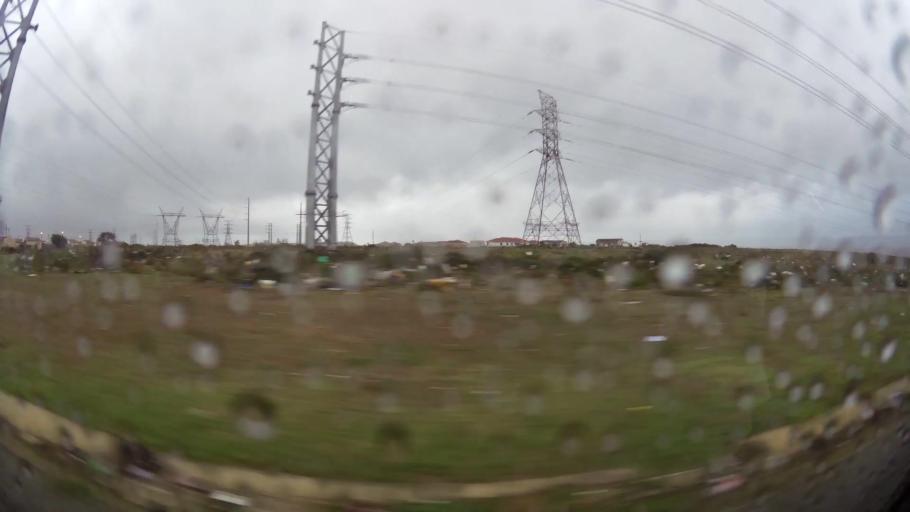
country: ZA
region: Eastern Cape
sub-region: Nelson Mandela Bay Metropolitan Municipality
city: Port Elizabeth
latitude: -33.8360
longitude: 25.5160
